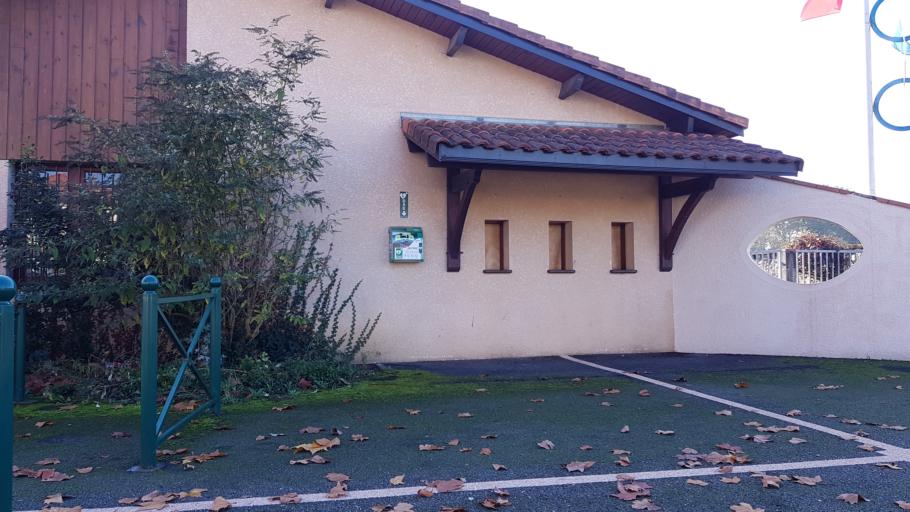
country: FR
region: Aquitaine
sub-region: Departement des Landes
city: Saint-Paul-les-Dax
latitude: 43.7267
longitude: -1.0597
